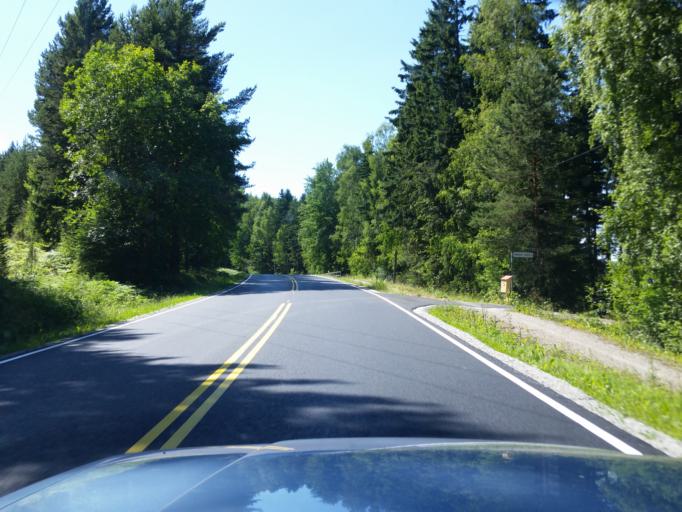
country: FI
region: Varsinais-Suomi
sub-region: Aboland-Turunmaa
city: Laensi-Turunmaa
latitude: 60.2429
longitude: 22.1366
